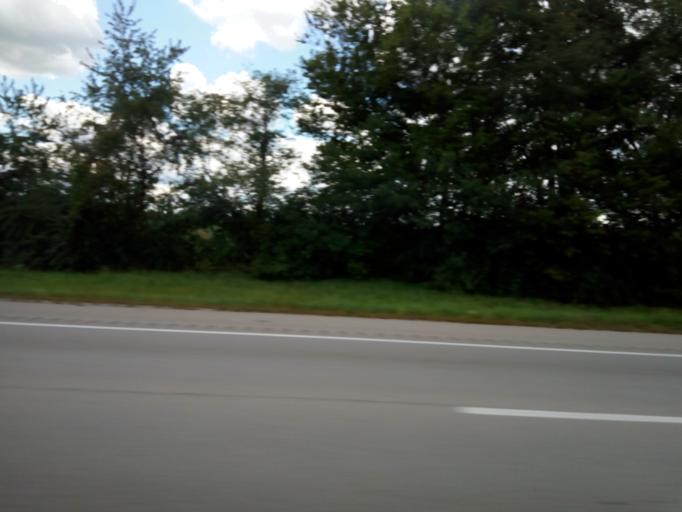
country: US
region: Kentucky
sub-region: Fayette County
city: Lexington
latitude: 37.9782
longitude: -84.3887
